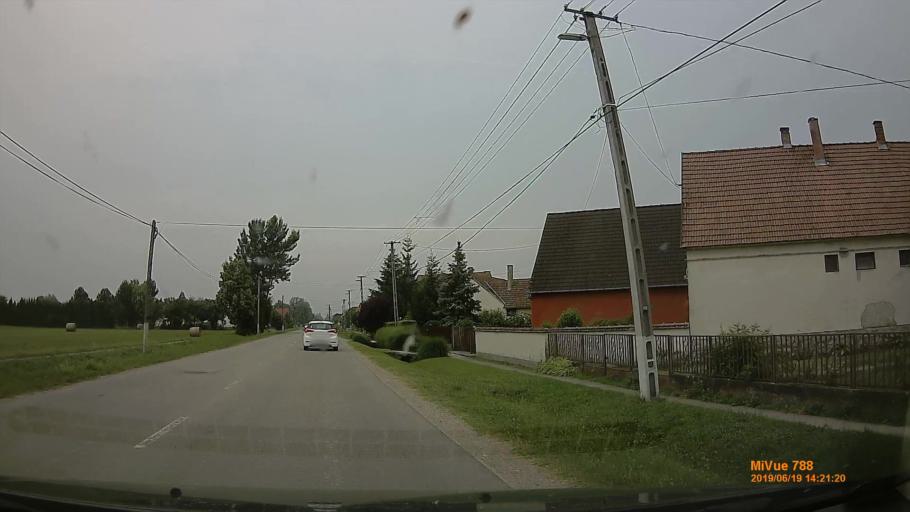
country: HU
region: Baranya
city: Szigetvar
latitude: 46.0199
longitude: 17.7726
